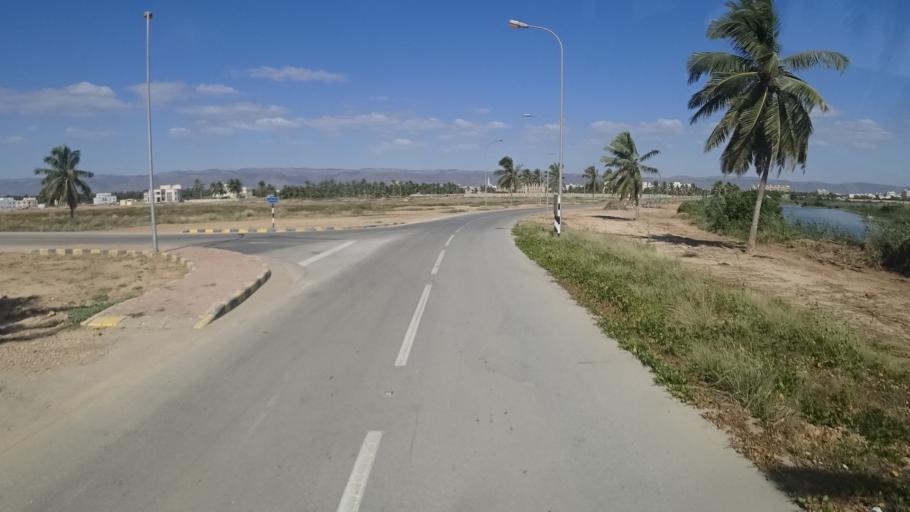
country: OM
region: Zufar
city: Salalah
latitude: 16.9963
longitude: 54.0655
